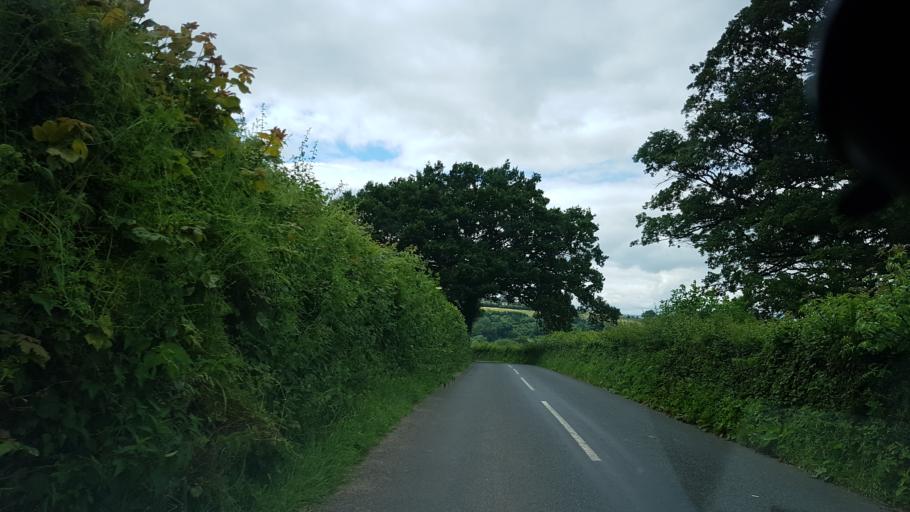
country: GB
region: Wales
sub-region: Monmouthshire
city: Grosmont
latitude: 51.9128
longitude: -2.8498
